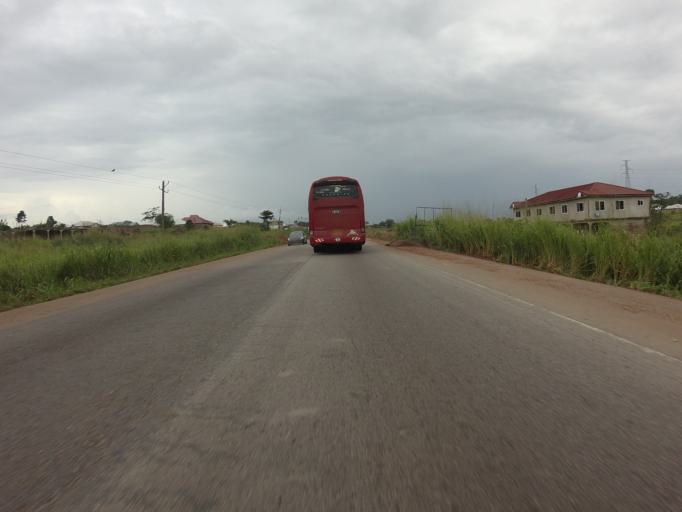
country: GH
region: Ashanti
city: Konongo
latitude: 6.6169
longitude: -1.1751
